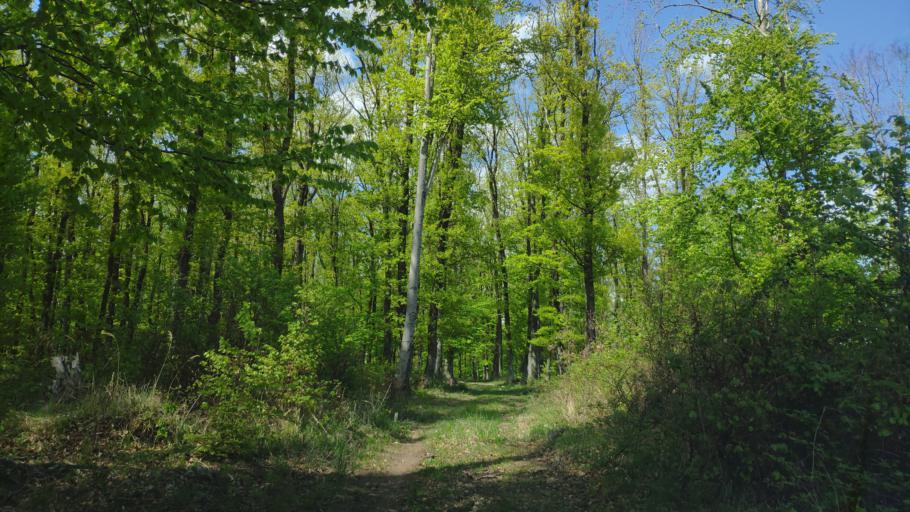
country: SK
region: Kosicky
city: Kosice
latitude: 48.6619
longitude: 21.4421
